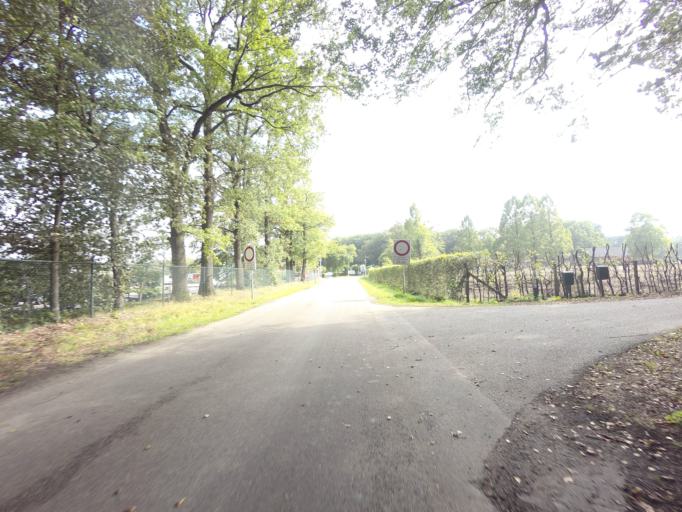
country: NL
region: Overijssel
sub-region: Gemeente Hengelo
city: Hengelo
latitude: 52.2671
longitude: 6.8421
